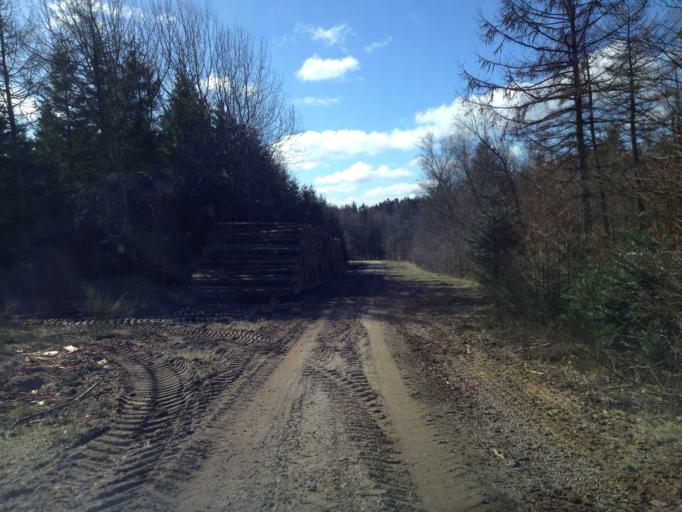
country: DK
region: Central Jutland
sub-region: Holstebro Kommune
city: Ulfborg
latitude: 56.2557
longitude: 8.4612
